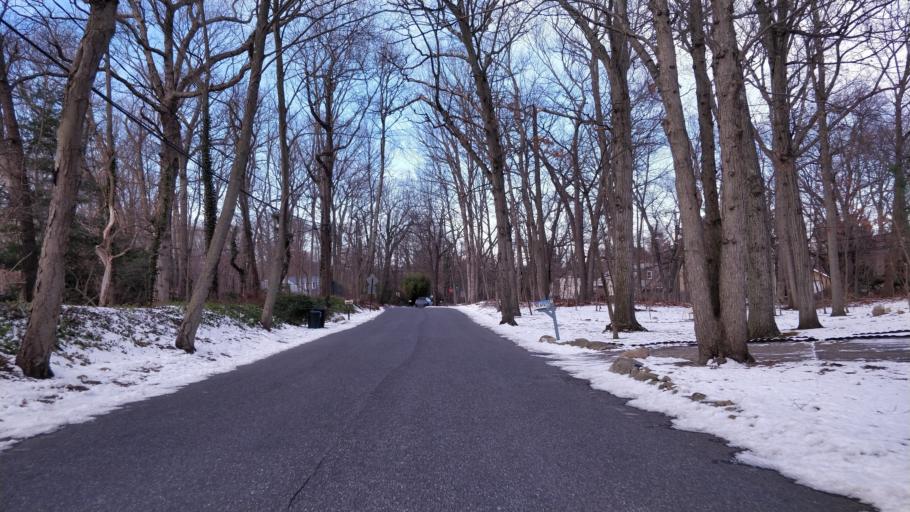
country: US
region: New York
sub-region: Suffolk County
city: Northport
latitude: 40.8866
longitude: -73.3439
